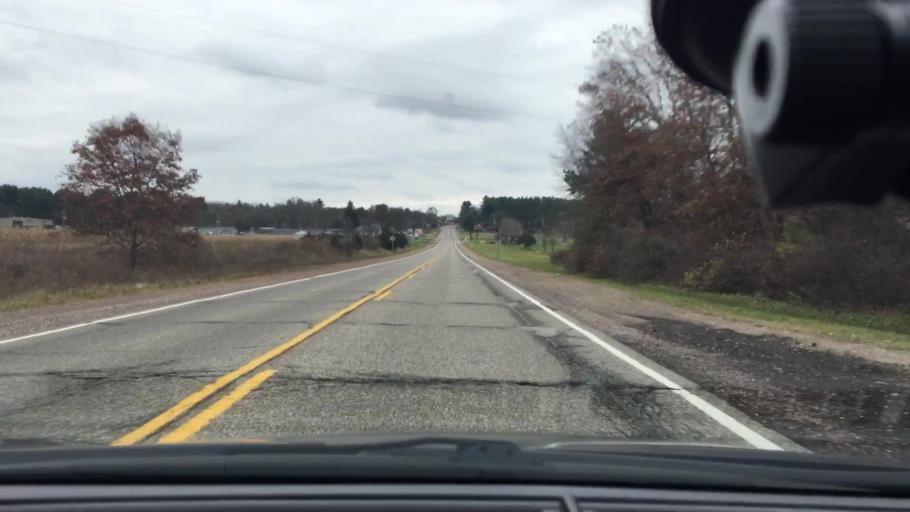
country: US
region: Wisconsin
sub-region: Columbia County
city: Wisconsin Dells
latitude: 43.6372
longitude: -89.7954
